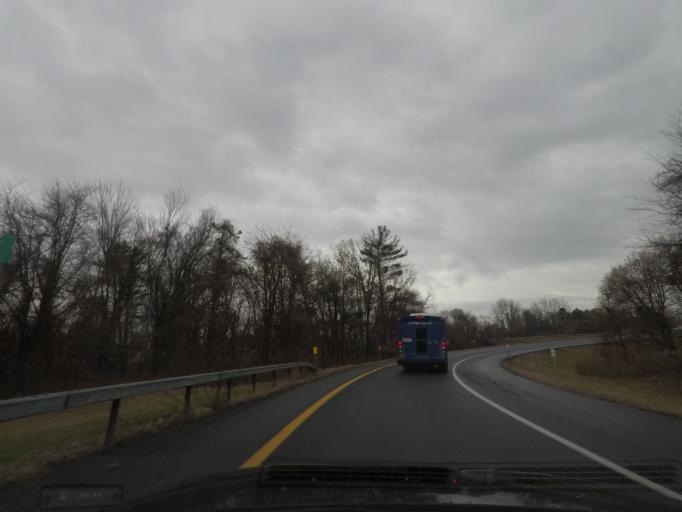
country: US
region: New York
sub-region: Albany County
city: Colonie
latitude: 42.7131
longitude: -73.8231
